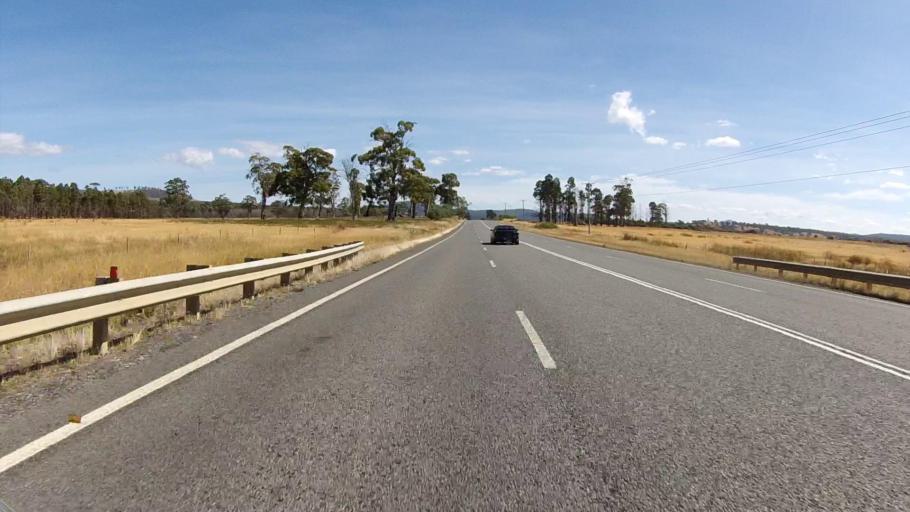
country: AU
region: Tasmania
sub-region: Sorell
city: Sorell
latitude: -42.6002
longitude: 147.7598
